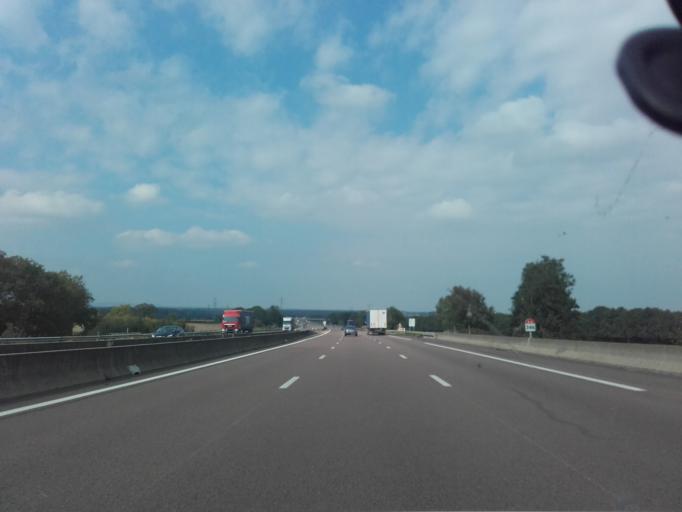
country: FR
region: Bourgogne
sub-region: Departement de Saone-et-Loire
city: Sennecey-le-Grand
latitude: 46.6550
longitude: 4.8577
